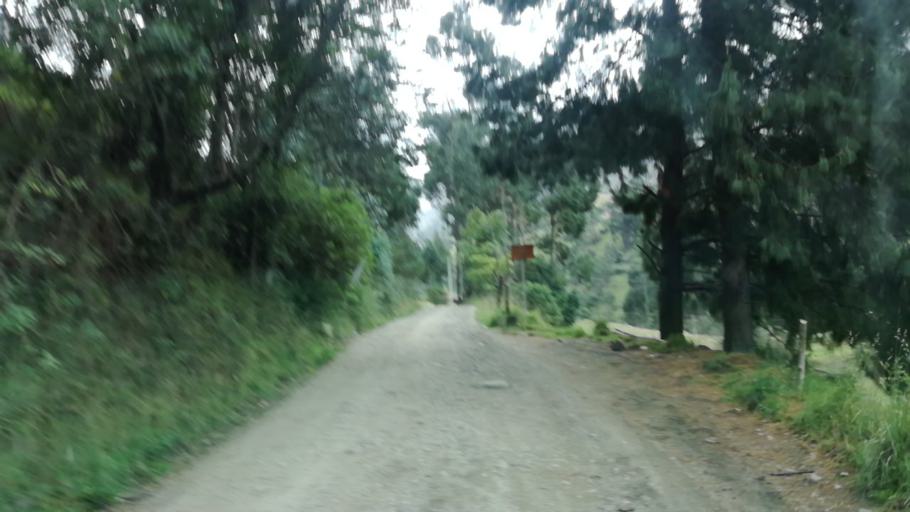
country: CO
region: Boyaca
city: Socha Viejo
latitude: 5.9404
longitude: -72.6892
